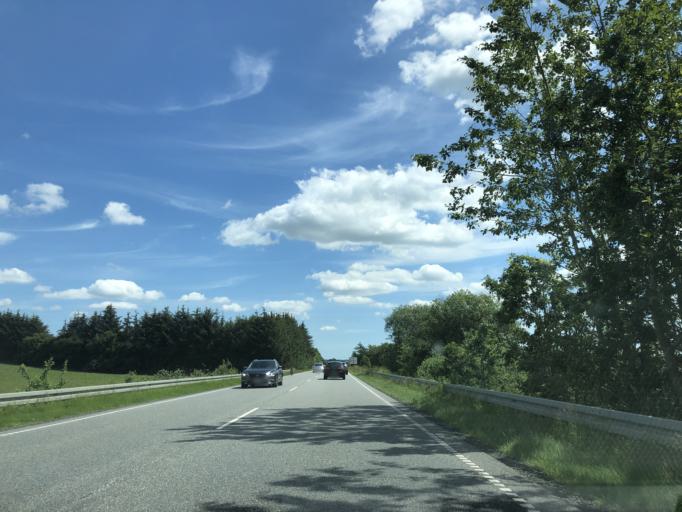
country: DK
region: Central Jutland
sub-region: Favrskov Kommune
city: Hammel
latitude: 56.2517
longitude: 9.7670
